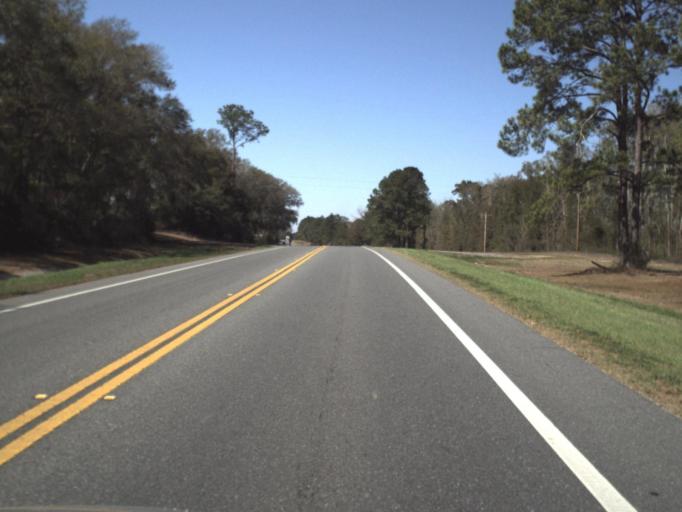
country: US
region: Florida
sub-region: Jackson County
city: Marianna
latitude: 30.7350
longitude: -85.1010
